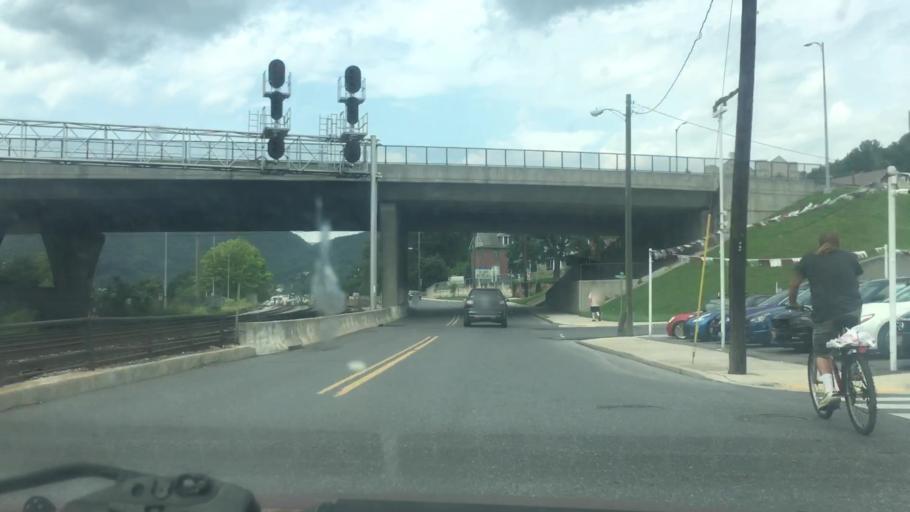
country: US
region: Maryland
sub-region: Allegany County
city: Cumberland
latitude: 39.6549
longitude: -78.7605
